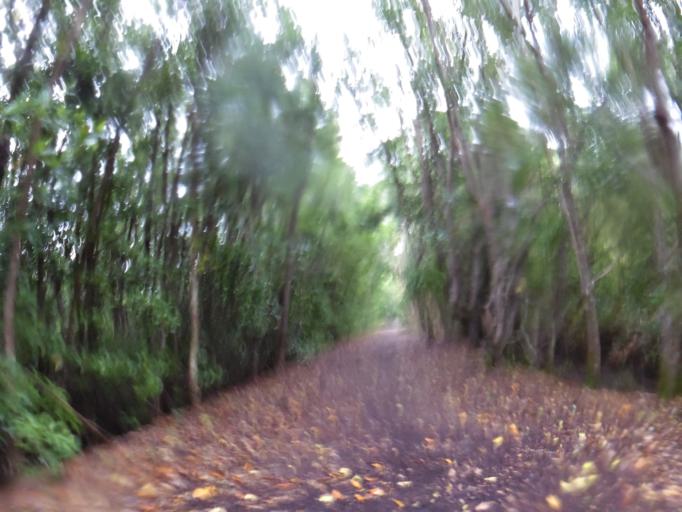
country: AU
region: Queensland
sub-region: Cairns
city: Cairns
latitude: -16.9005
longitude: 145.7533
